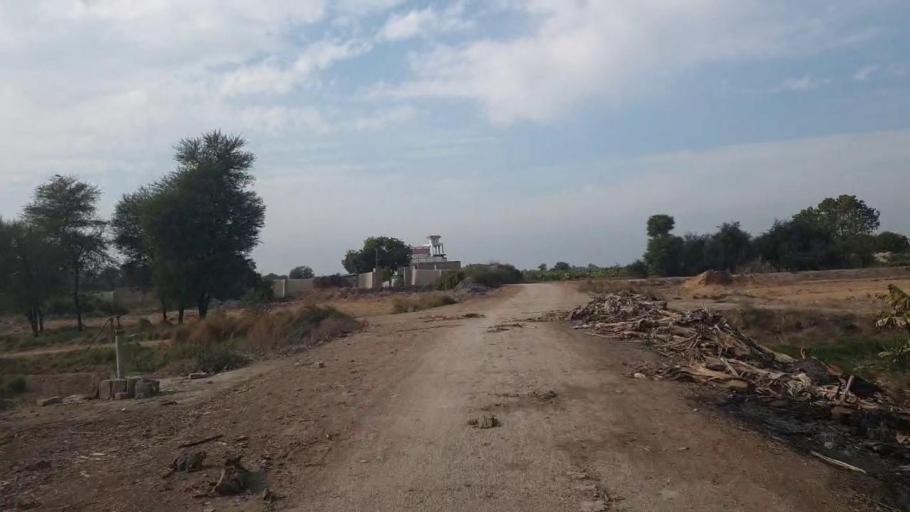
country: PK
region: Sindh
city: Shahdadpur
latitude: 26.0185
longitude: 68.5229
